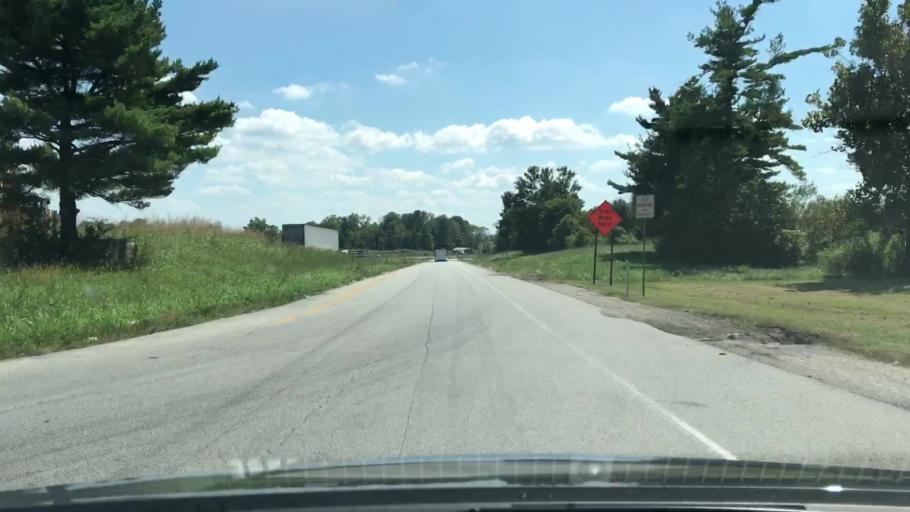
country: US
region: Kentucky
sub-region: Hardin County
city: Elizabethtown
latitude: 37.5965
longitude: -85.8708
